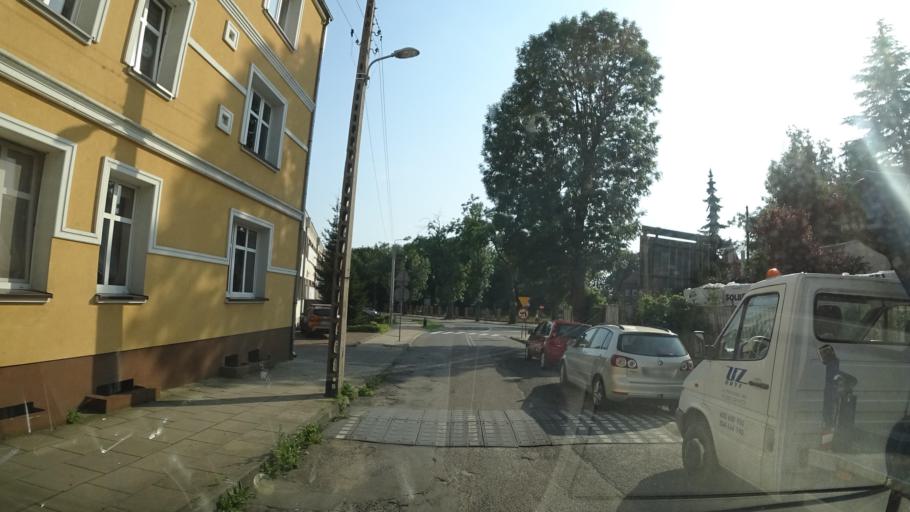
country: PL
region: West Pomeranian Voivodeship
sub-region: Powiat gryficki
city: Gryfice
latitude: 53.9191
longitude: 15.2007
